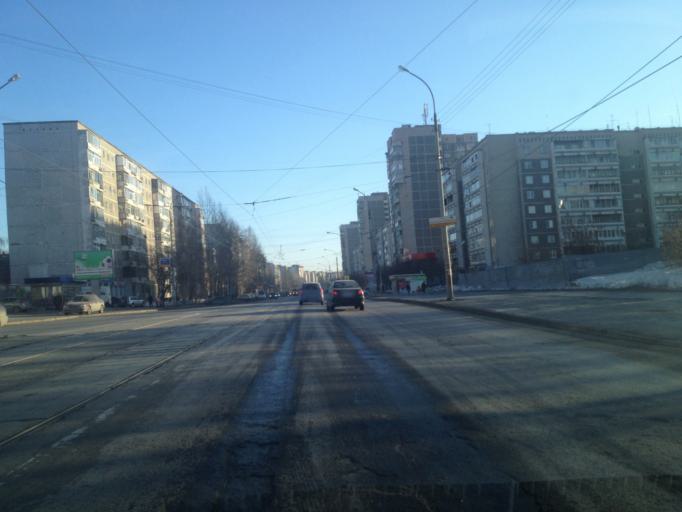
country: RU
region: Sverdlovsk
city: Yekaterinburg
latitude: 56.8359
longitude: 60.5457
